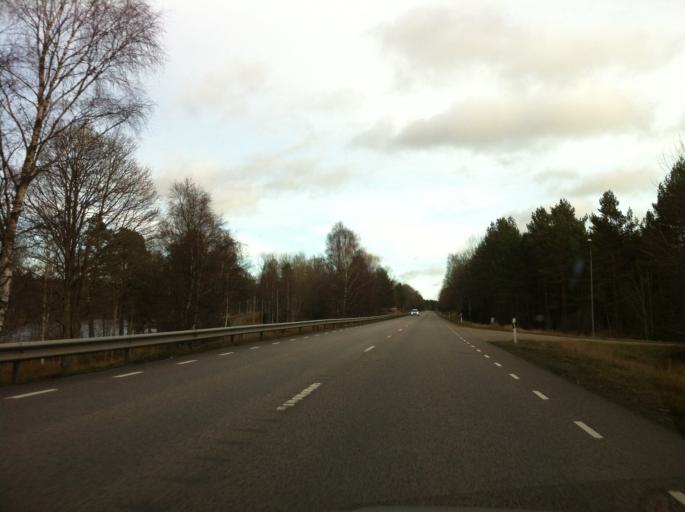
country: SE
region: Kronoberg
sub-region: Uppvidinge Kommun
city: Aseda
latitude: 57.1378
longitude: 15.2829
